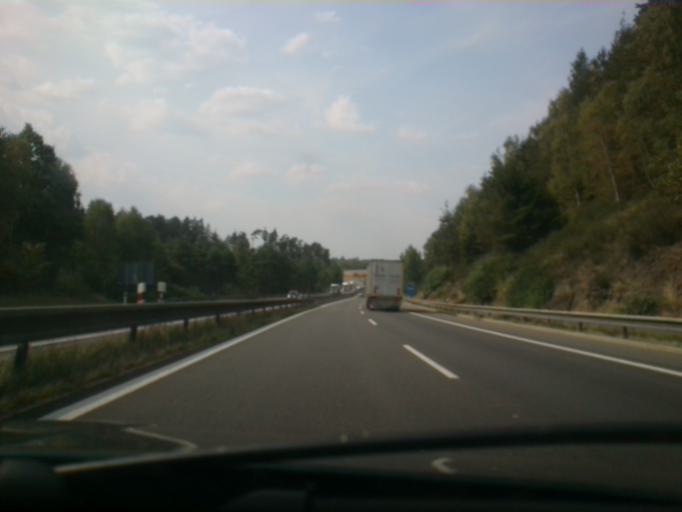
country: CZ
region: Central Bohemia
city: Trhovy Stepanov
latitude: 49.7458
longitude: 15.0307
